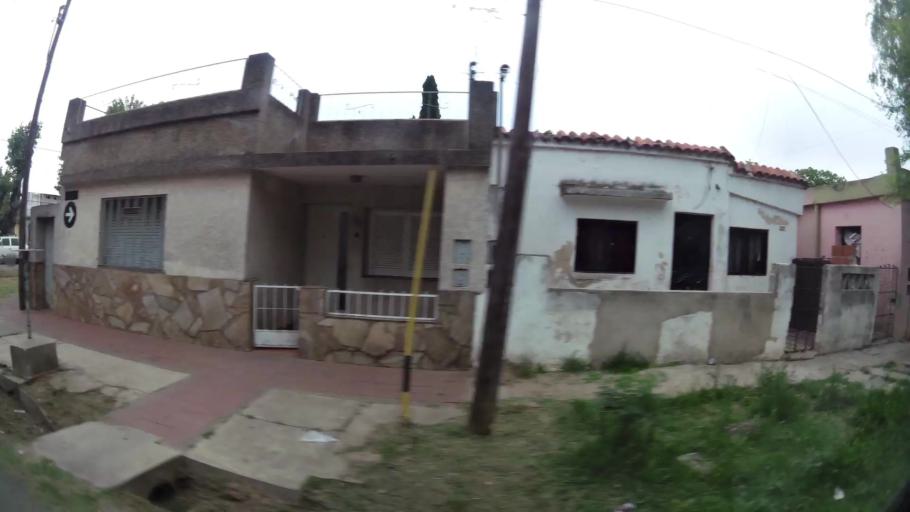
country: AR
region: Santa Fe
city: Granadero Baigorria
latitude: -32.8990
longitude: -60.7026
